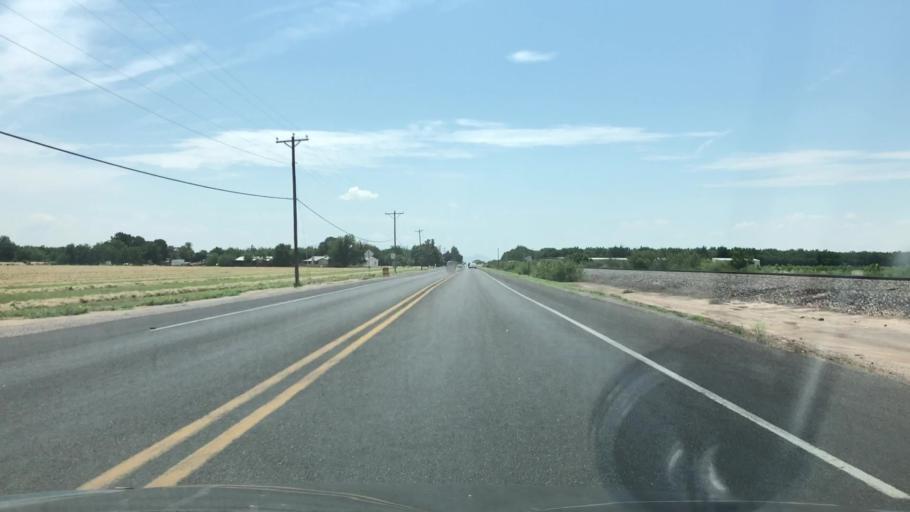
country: US
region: New Mexico
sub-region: Dona Ana County
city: Mesquite
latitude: 32.2087
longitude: -106.7245
